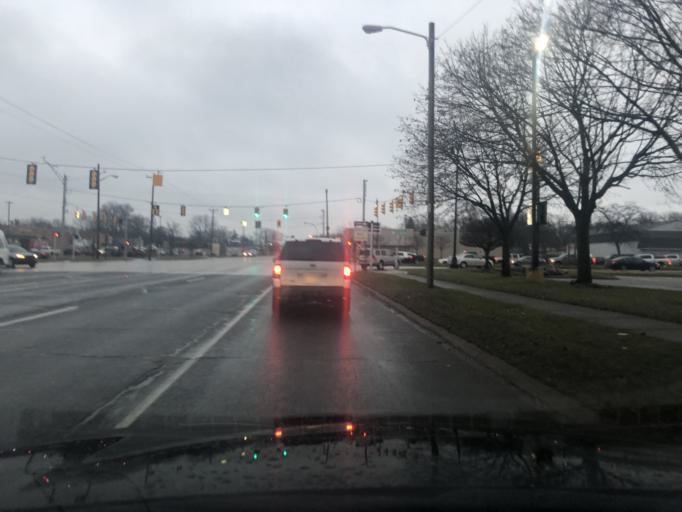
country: US
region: Michigan
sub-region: Wayne County
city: Taylor
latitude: 42.2690
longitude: -83.2713
